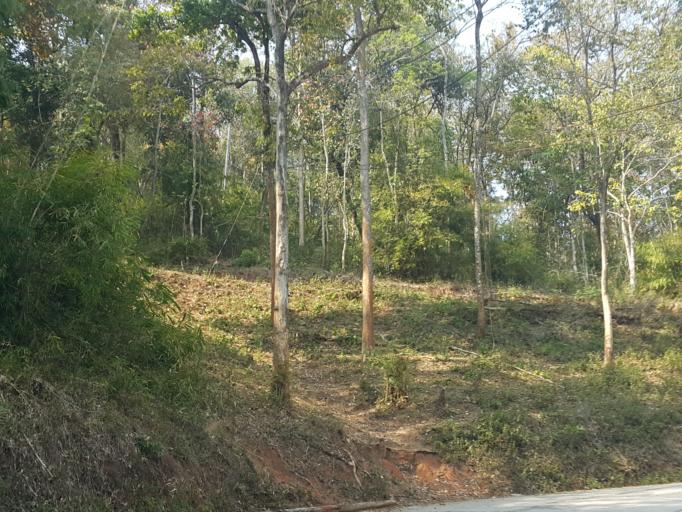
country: TH
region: Chiang Mai
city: Mae Taeng
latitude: 19.0181
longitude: 98.8034
